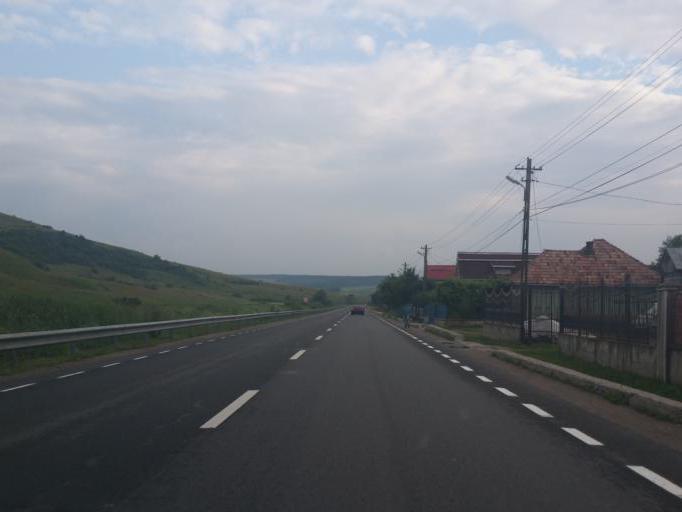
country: RO
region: Cluj
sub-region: Comuna Sanpaul
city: Sanpaul
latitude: 46.8660
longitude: 23.4114
